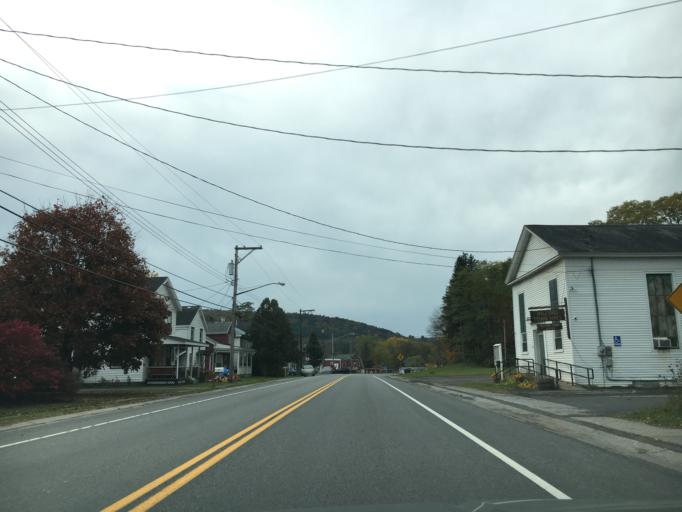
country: US
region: New York
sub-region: Otsego County
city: Oneonta
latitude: 42.5306
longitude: -74.9674
